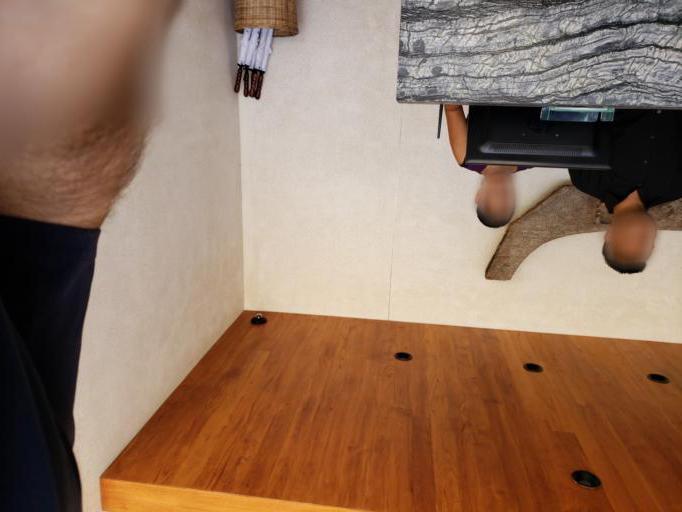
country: ID
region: Bali
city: Kangin
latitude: -8.8460
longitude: 115.1408
